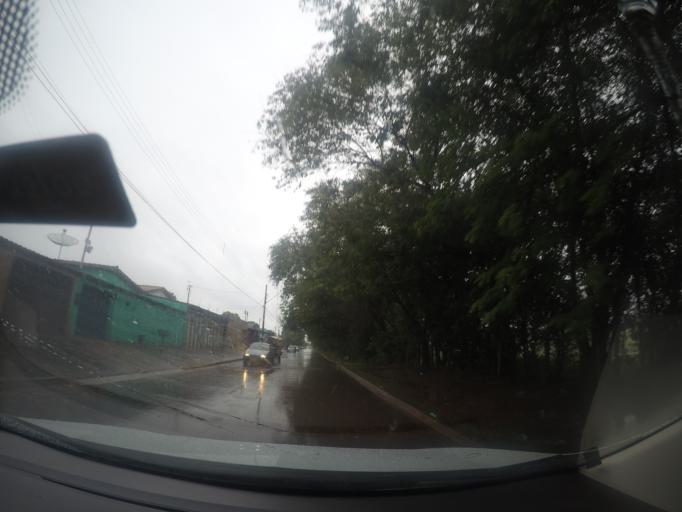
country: BR
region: Goias
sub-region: Goianira
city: Goianira
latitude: -16.5941
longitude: -49.3541
